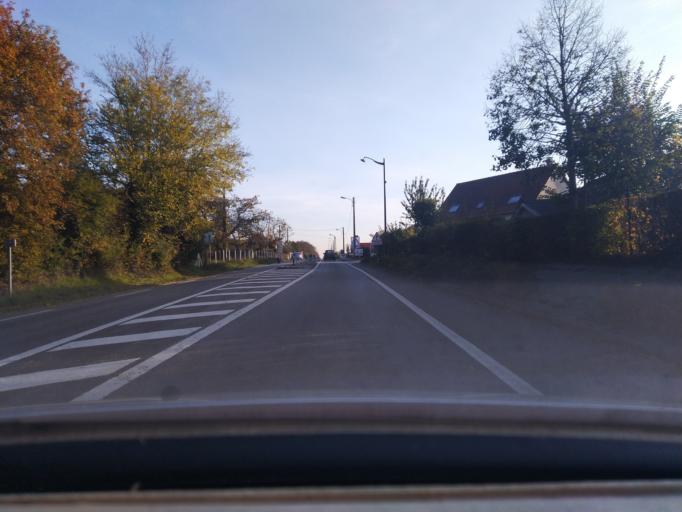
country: FR
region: Haute-Normandie
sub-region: Departement de la Seine-Maritime
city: Le Trait
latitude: 49.4693
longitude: 0.8170
